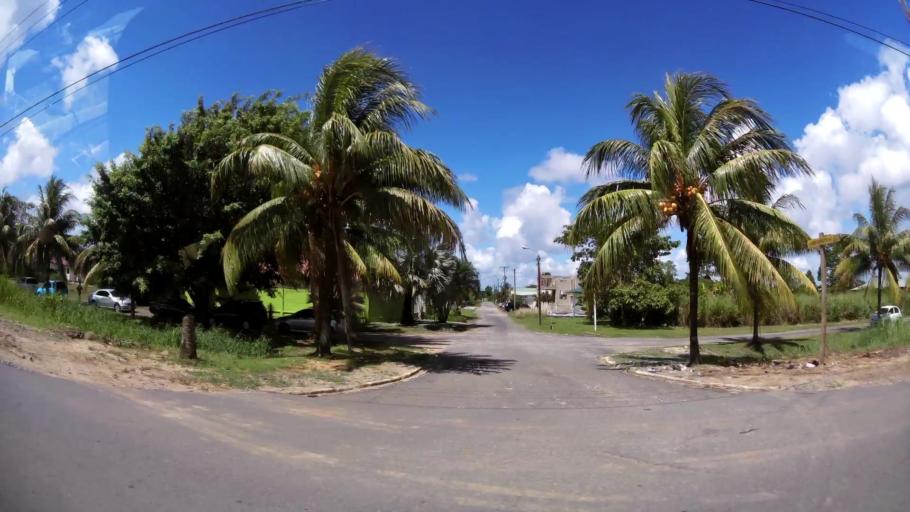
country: SR
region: Paramaribo
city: Paramaribo
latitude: 5.8637
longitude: -55.1276
